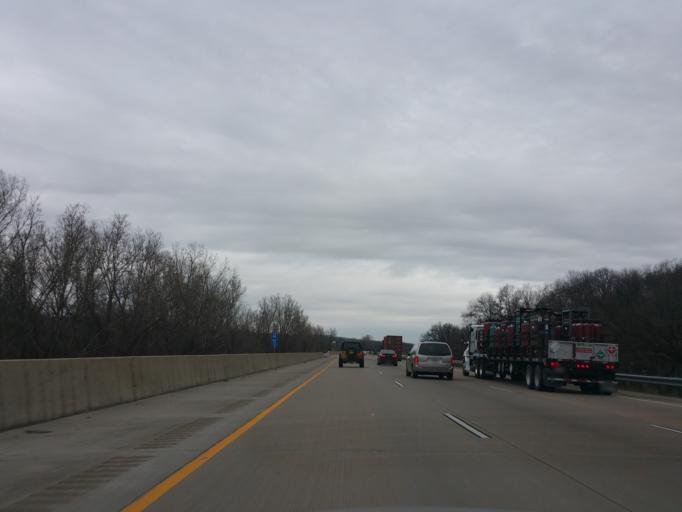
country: US
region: Wisconsin
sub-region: Columbia County
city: Poynette
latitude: 43.3788
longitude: -89.4623
